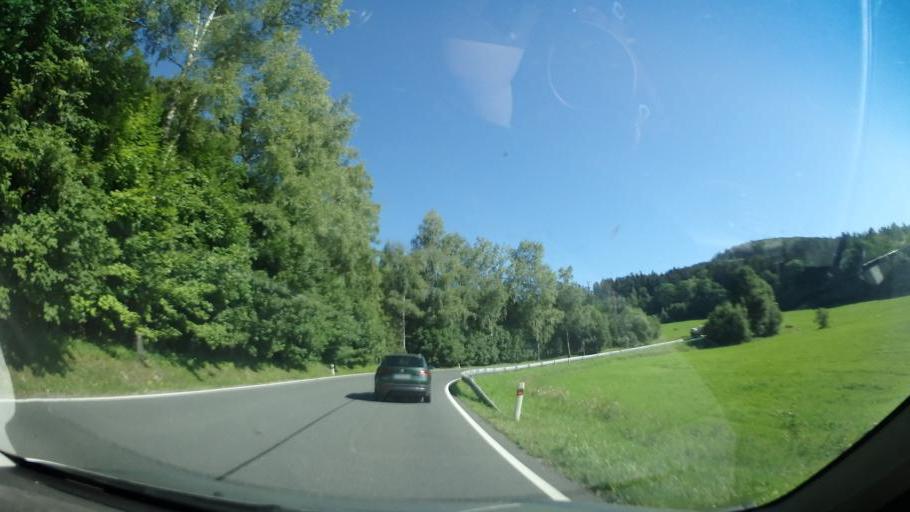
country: CZ
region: Olomoucky
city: Vapenna
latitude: 50.2412
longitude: 17.1428
